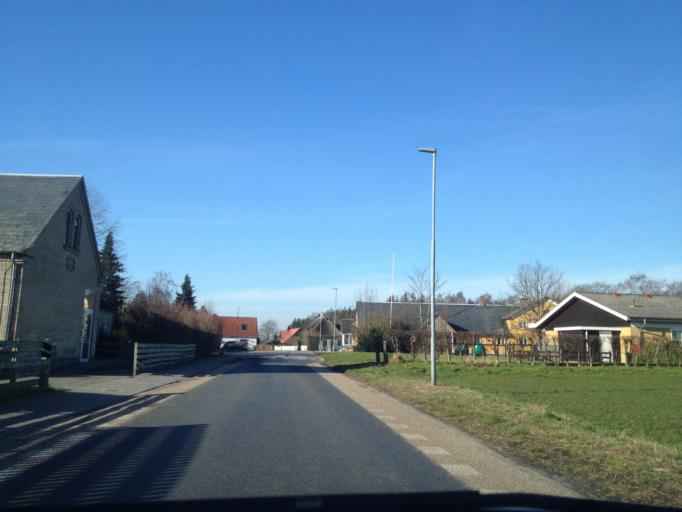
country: DK
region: South Denmark
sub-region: Nyborg Kommune
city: Ullerslev
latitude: 55.3940
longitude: 10.6896
